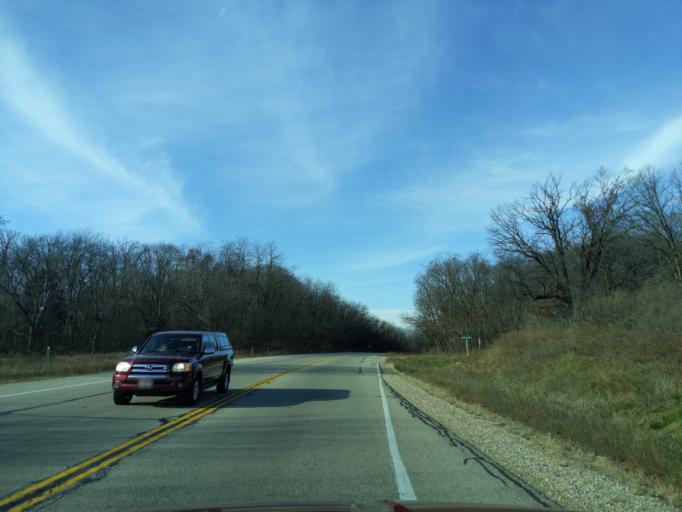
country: US
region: Wisconsin
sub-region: Walworth County
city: Whitewater
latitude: 42.7994
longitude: -88.6455
